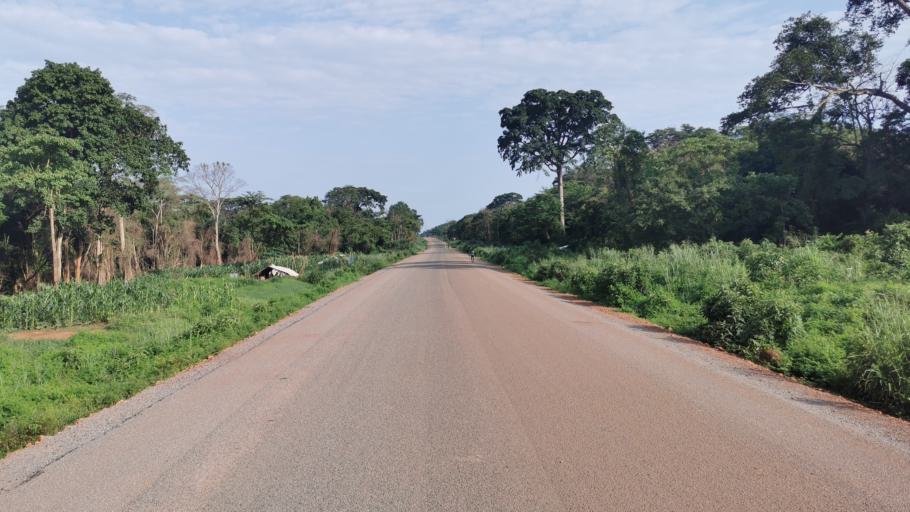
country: ET
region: Gambela
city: Gambela
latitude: 7.6905
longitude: 34.6692
